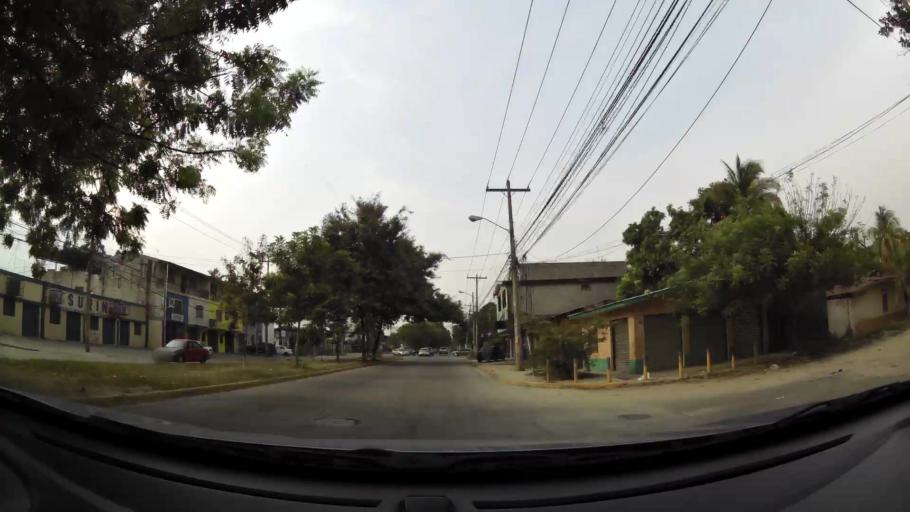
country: HN
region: Cortes
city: San Pedro Sula
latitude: 15.5197
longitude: -88.0167
